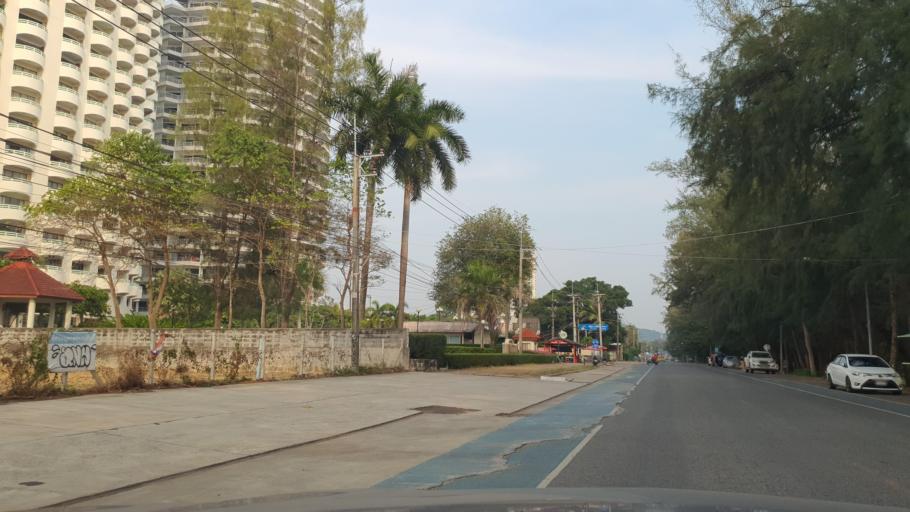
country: TH
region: Rayong
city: Rayong
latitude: 12.6032
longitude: 101.3994
